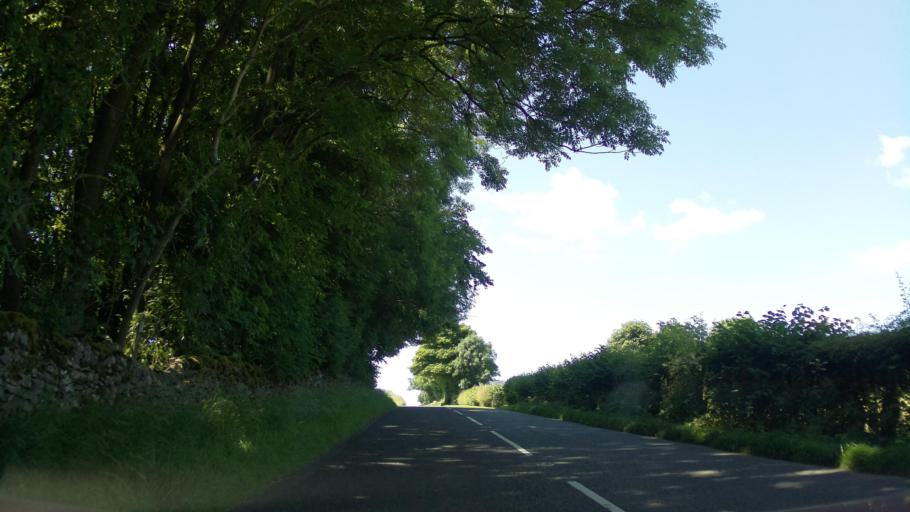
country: GB
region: England
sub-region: Derbyshire
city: Bakewell
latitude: 53.2058
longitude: -1.7031
